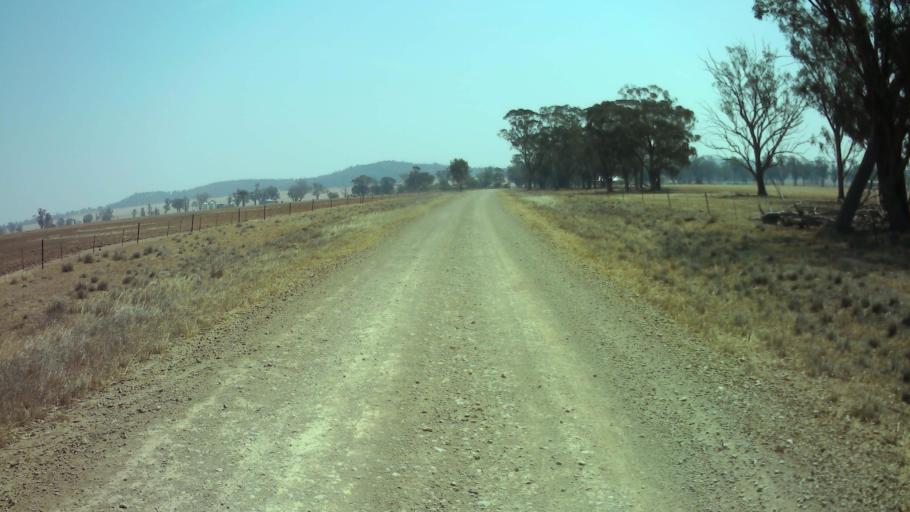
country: AU
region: New South Wales
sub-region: Weddin
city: Grenfell
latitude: -33.6408
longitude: 148.2523
